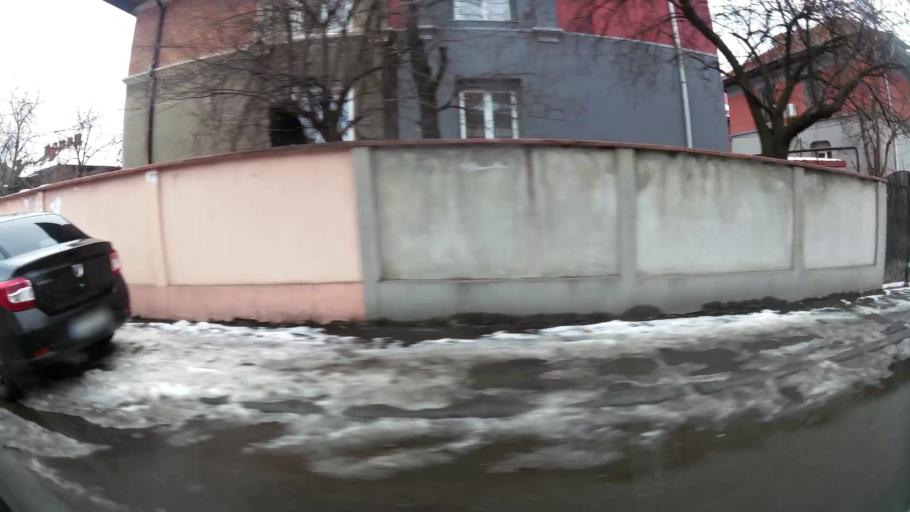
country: RO
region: Bucuresti
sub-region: Municipiul Bucuresti
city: Bucuresti
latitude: 44.4238
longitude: 26.0591
